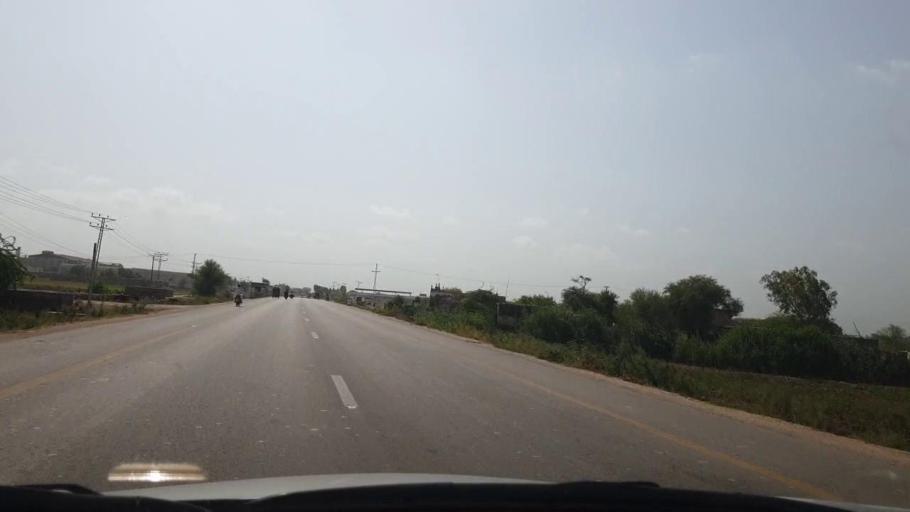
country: PK
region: Sindh
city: Matli
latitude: 25.0000
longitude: 68.6518
